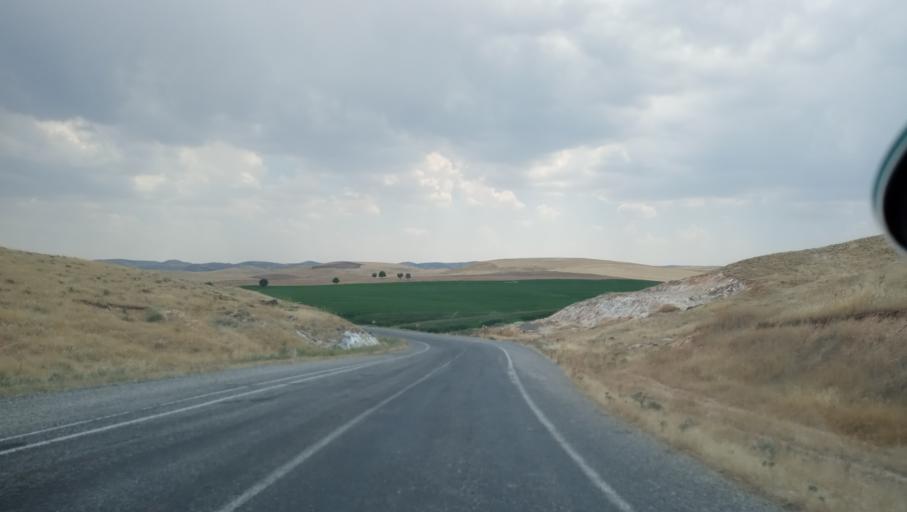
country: TR
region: Mardin
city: Baskavak
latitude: 37.6765
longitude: 40.8503
